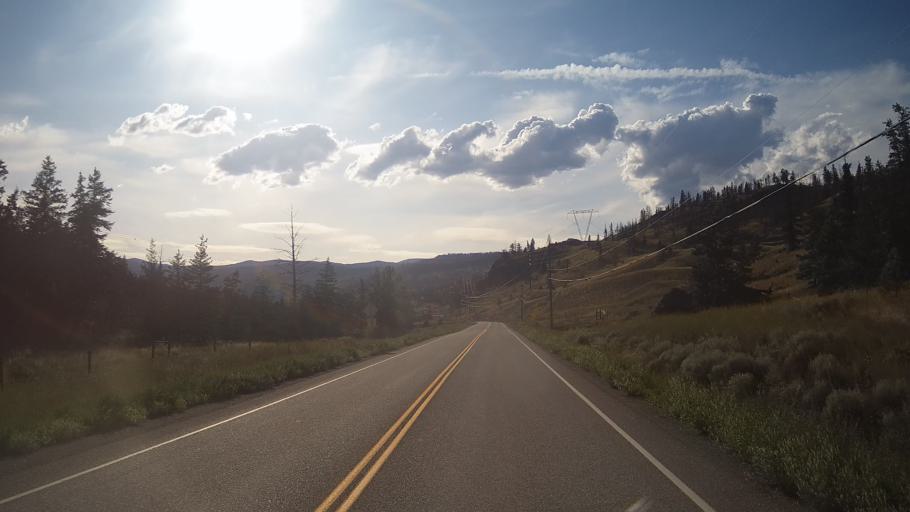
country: CA
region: British Columbia
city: Cache Creek
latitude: 50.8845
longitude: -121.4284
